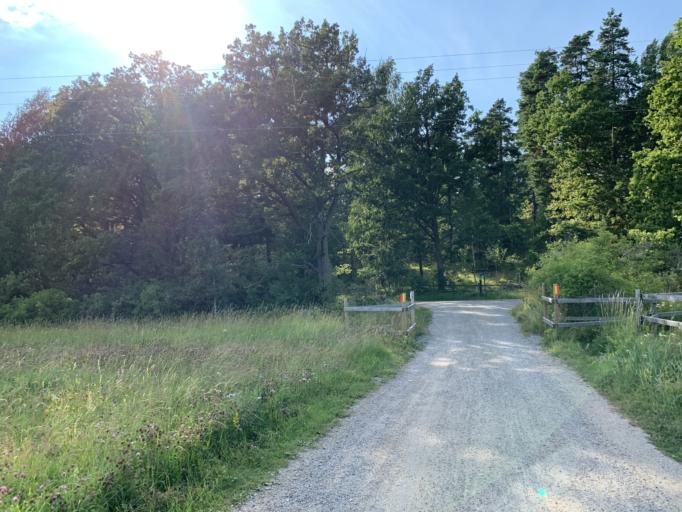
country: SE
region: Stockholm
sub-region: Jarfalla Kommun
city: Jakobsberg
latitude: 59.4426
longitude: 17.8575
